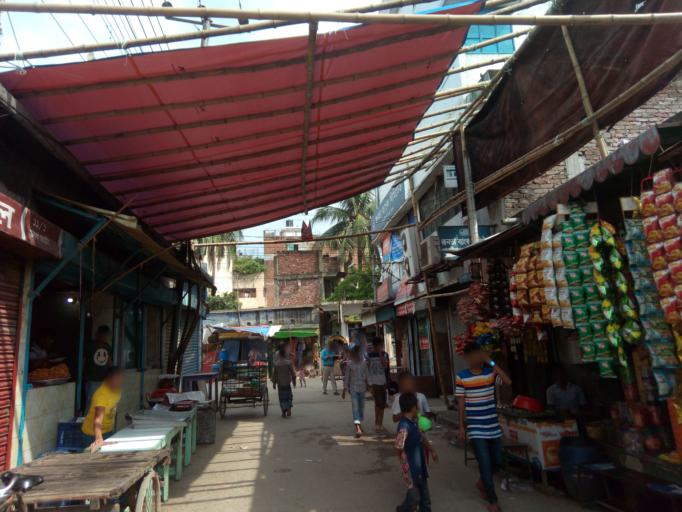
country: BD
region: Dhaka
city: Azimpur
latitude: 23.7329
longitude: 90.3667
